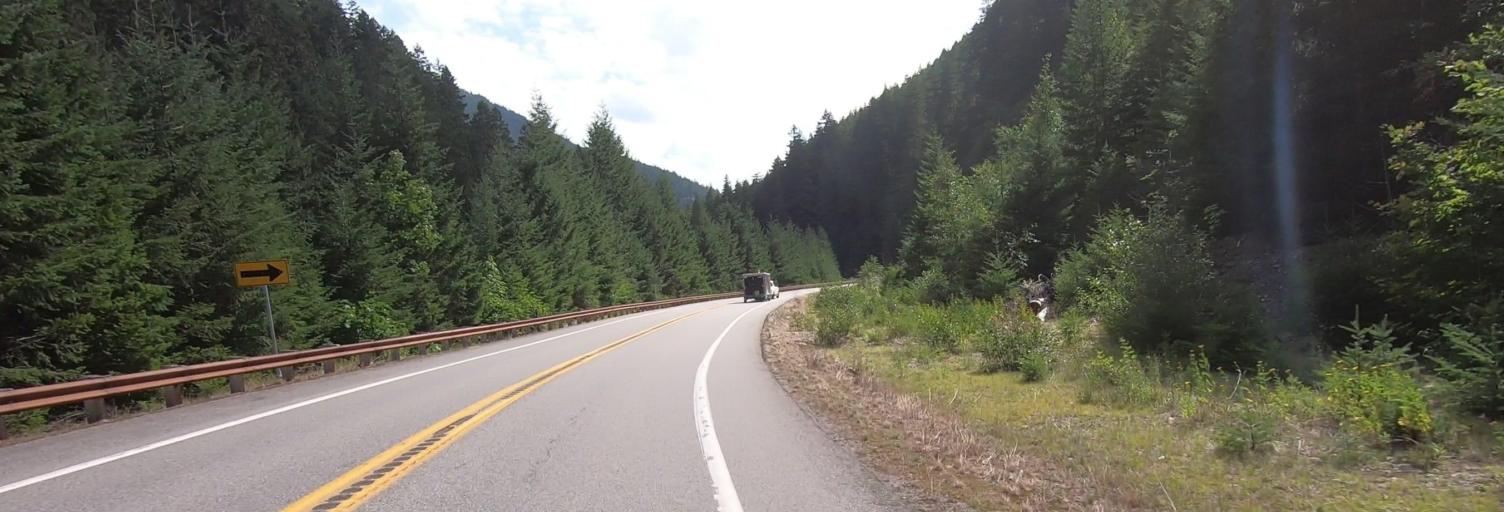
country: US
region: Washington
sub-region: Snohomish County
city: Darrington
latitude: 48.6860
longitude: -120.8989
